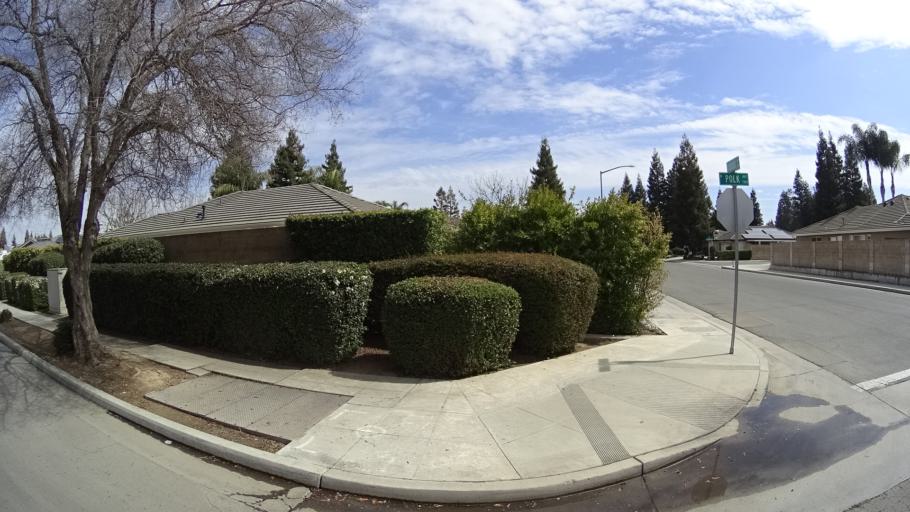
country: US
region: California
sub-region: Fresno County
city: Biola
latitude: 36.8397
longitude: -119.8882
